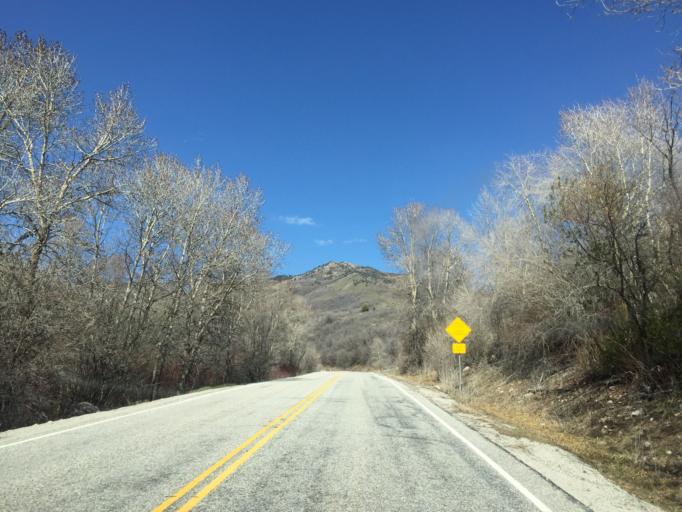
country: US
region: Utah
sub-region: Weber County
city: Wolf Creek
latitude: 41.3433
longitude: -111.8235
